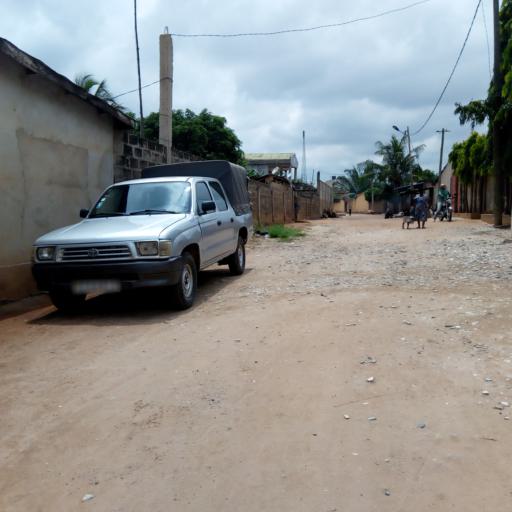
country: TG
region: Maritime
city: Lome
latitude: 6.1738
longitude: 1.1790
